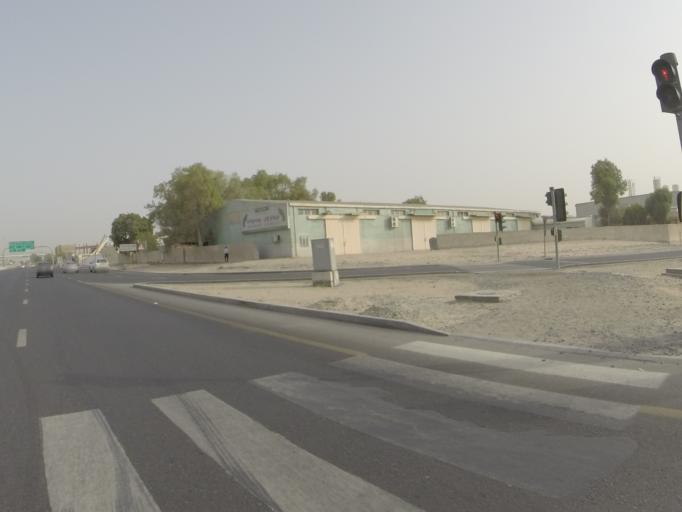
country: AE
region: Dubai
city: Dubai
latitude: 25.1454
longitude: 55.2302
